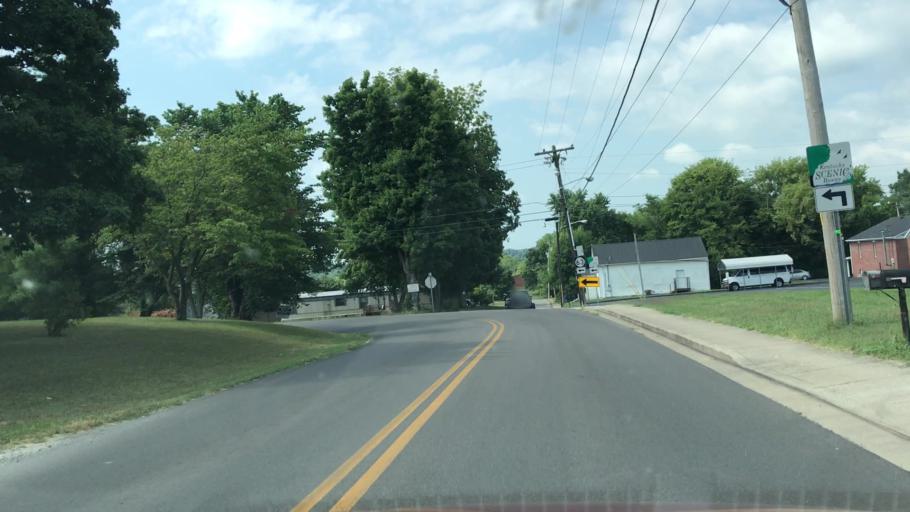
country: US
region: Kentucky
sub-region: Barren County
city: Glasgow
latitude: 36.9903
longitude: -85.9102
